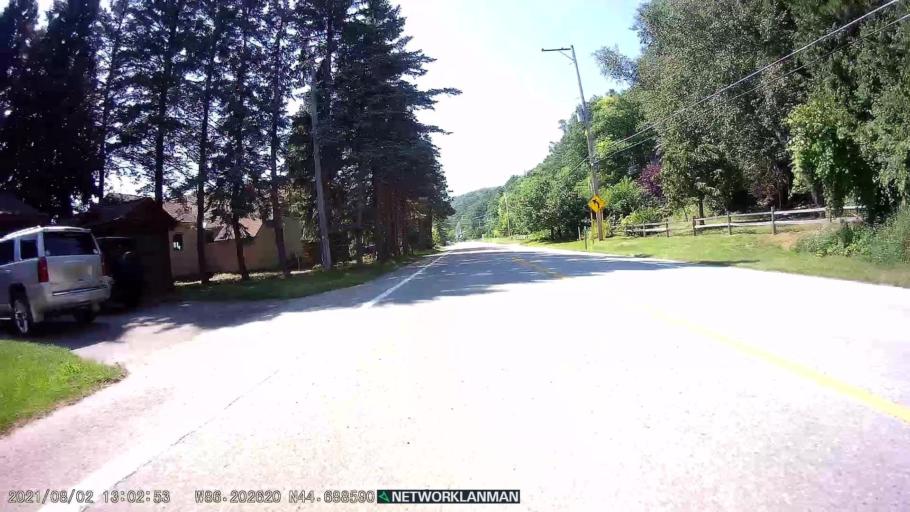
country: US
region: Michigan
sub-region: Benzie County
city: Frankfort
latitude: 44.6887
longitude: -86.2028
